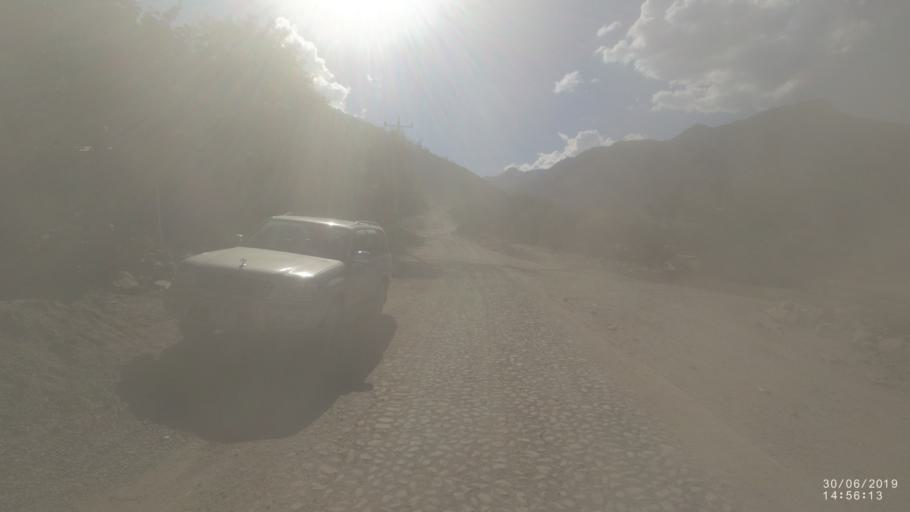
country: BO
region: Cochabamba
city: Irpa Irpa
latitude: -17.7503
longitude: -66.3529
